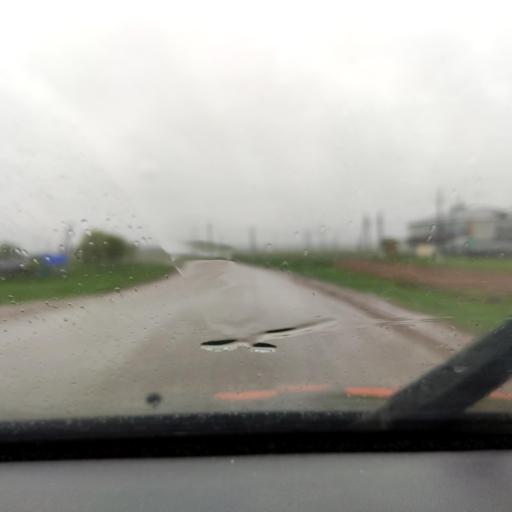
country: RU
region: Bashkortostan
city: Asanovo
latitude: 54.7647
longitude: 55.4891
